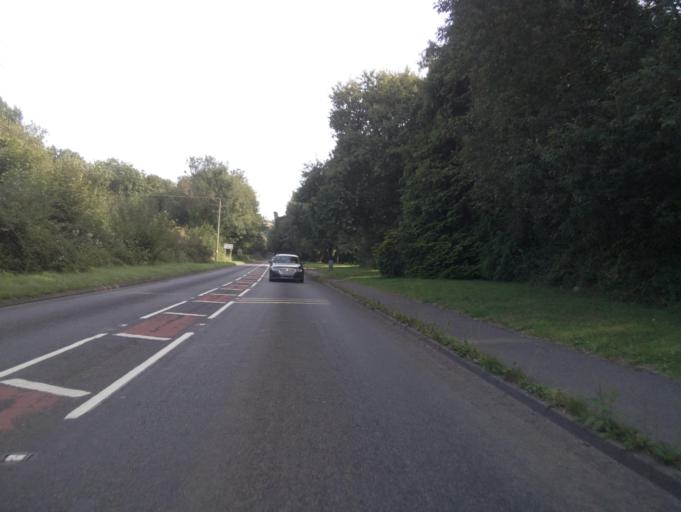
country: GB
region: England
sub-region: Devon
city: Tiverton
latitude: 50.8883
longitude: -3.4959
